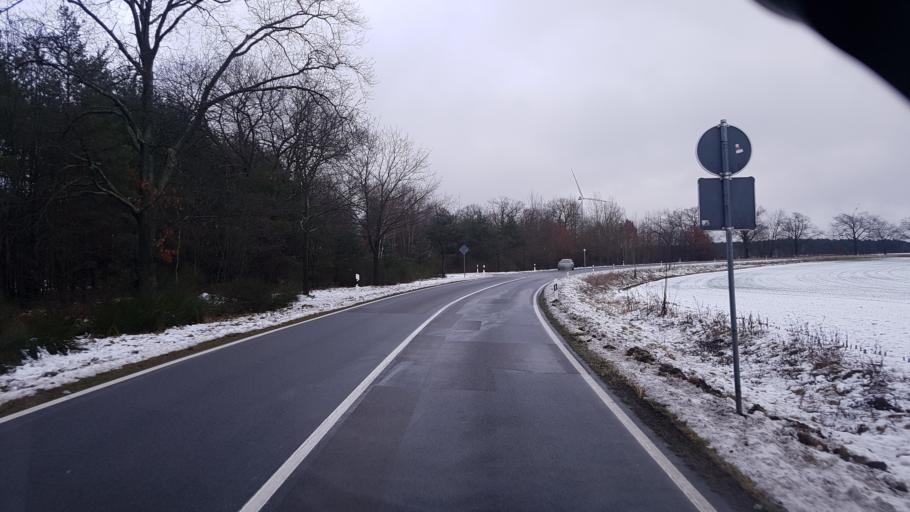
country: DE
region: Brandenburg
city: Schenkendobern
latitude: 51.9691
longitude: 14.5832
